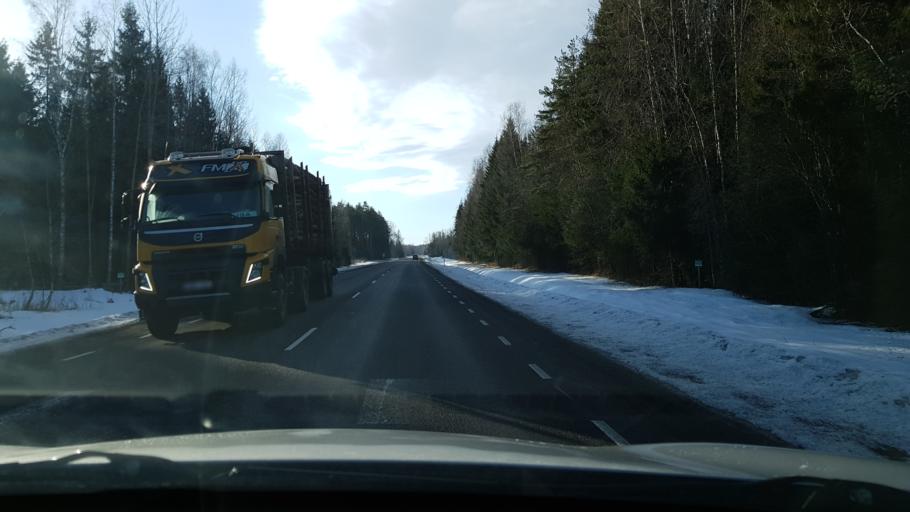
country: EE
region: Viljandimaa
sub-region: Vohma linn
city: Vohma
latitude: 58.5948
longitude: 25.5721
